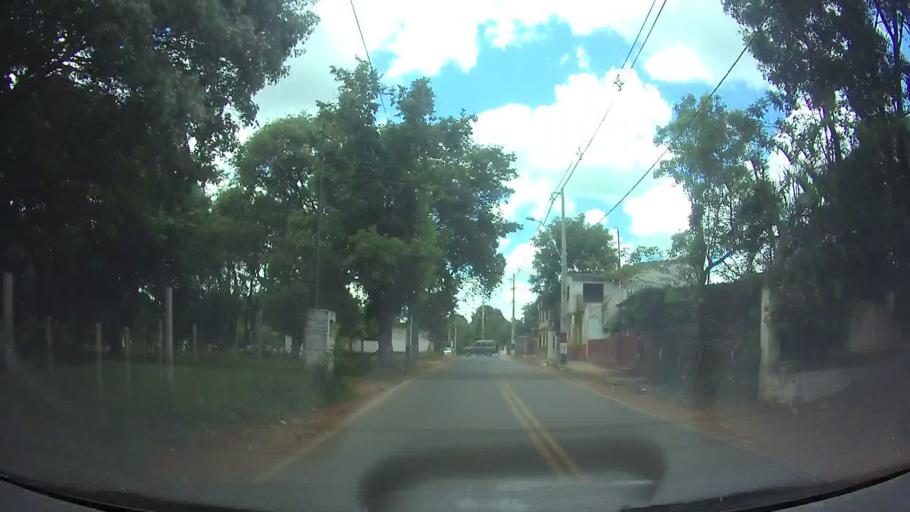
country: PY
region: Central
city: Capiata
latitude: -25.3002
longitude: -57.4417
